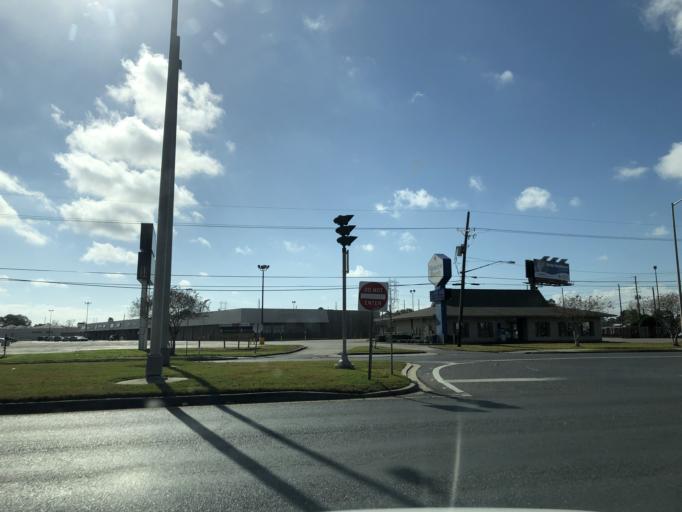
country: US
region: Louisiana
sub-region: Jefferson Parish
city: Kenner
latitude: 30.0054
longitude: -90.2191
